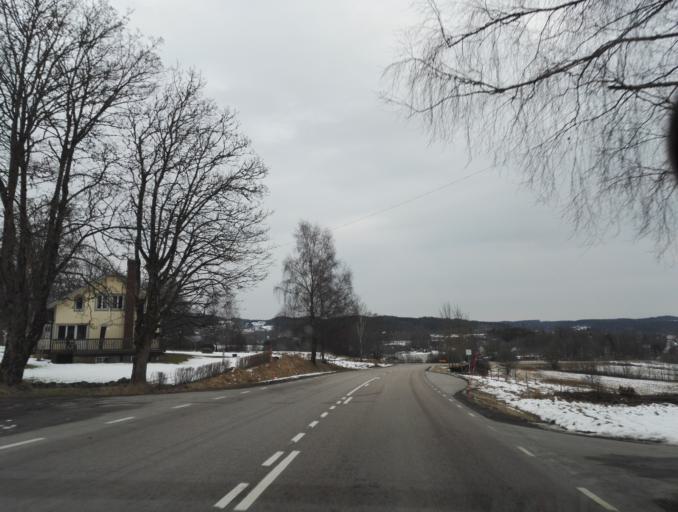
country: SE
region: Vaestra Goetaland
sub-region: Bollebygds Kommun
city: Bollebygd
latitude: 57.6749
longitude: 12.5445
